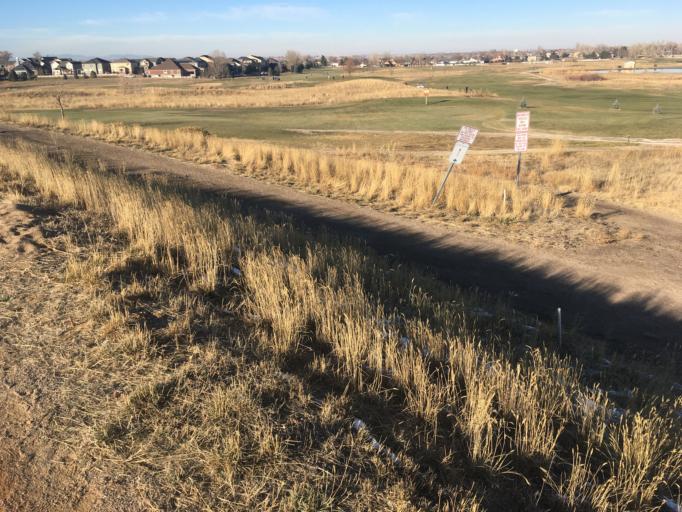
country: US
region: Colorado
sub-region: Weld County
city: Firestone
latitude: 40.1245
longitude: -104.9455
